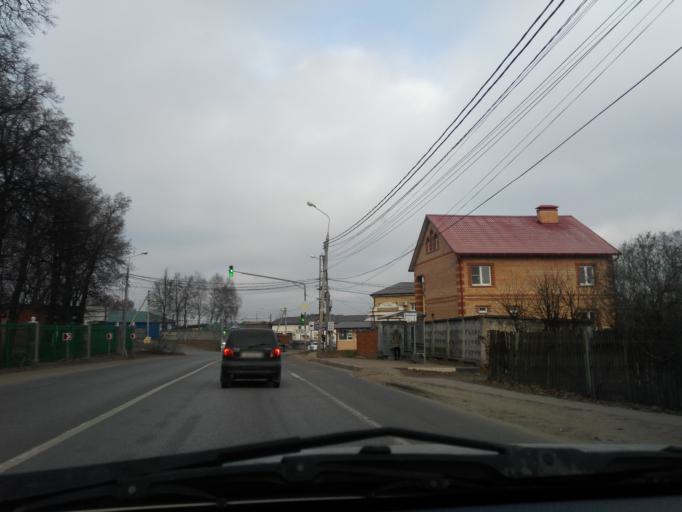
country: RU
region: Moskovskaya
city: Troitsk
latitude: 55.3178
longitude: 37.1538
